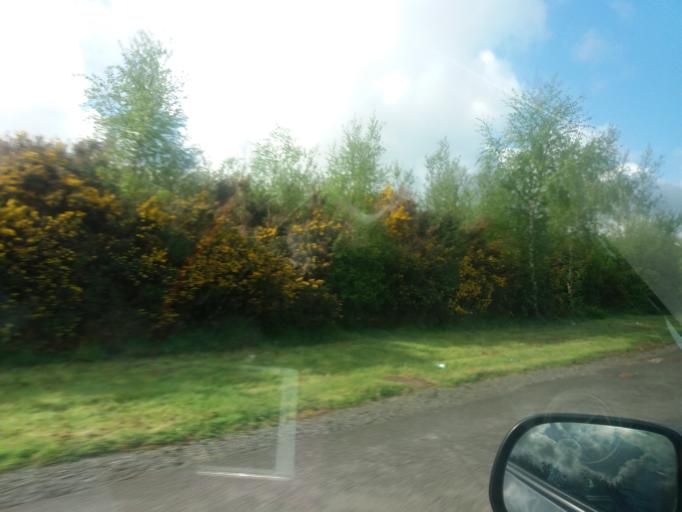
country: IE
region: Leinster
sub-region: Loch Garman
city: Gorey
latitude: 52.6560
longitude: -6.3004
